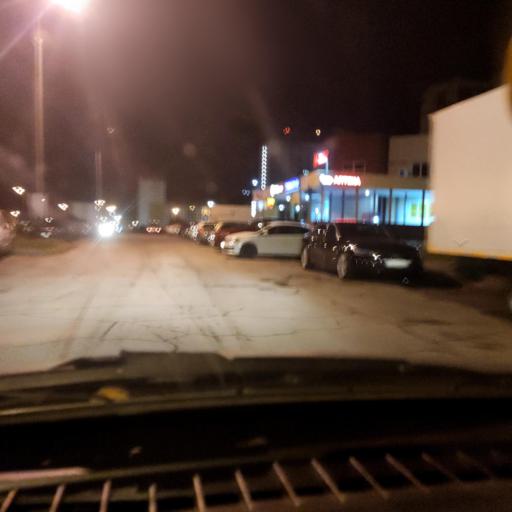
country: RU
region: Samara
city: Tol'yatti
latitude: 53.4998
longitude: 49.2778
